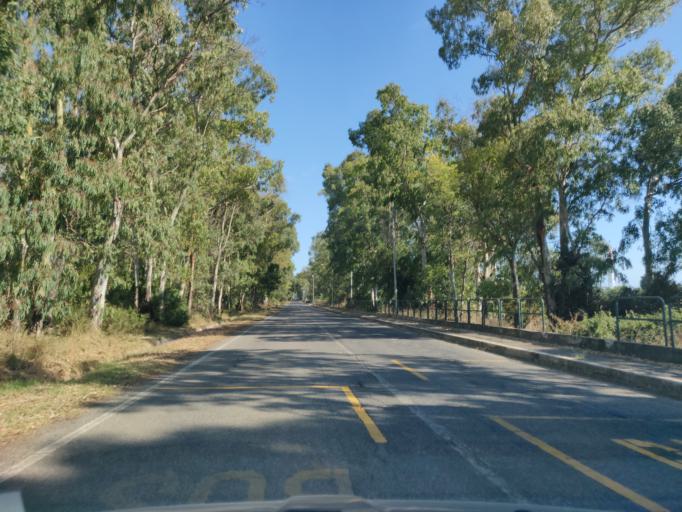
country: IT
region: Latium
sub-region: Citta metropolitana di Roma Capitale
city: Aurelia
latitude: 42.1491
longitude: 11.7600
